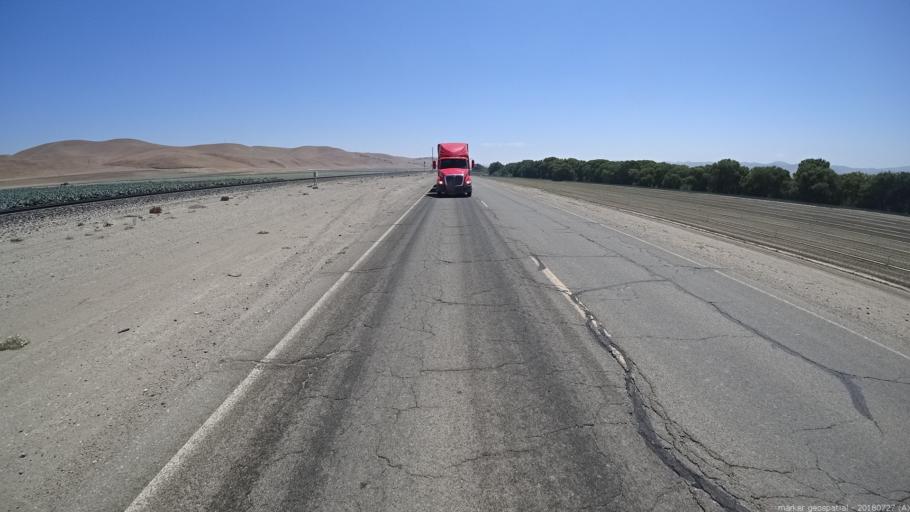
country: US
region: California
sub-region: Monterey County
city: King City
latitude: 36.0663
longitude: -120.9316
